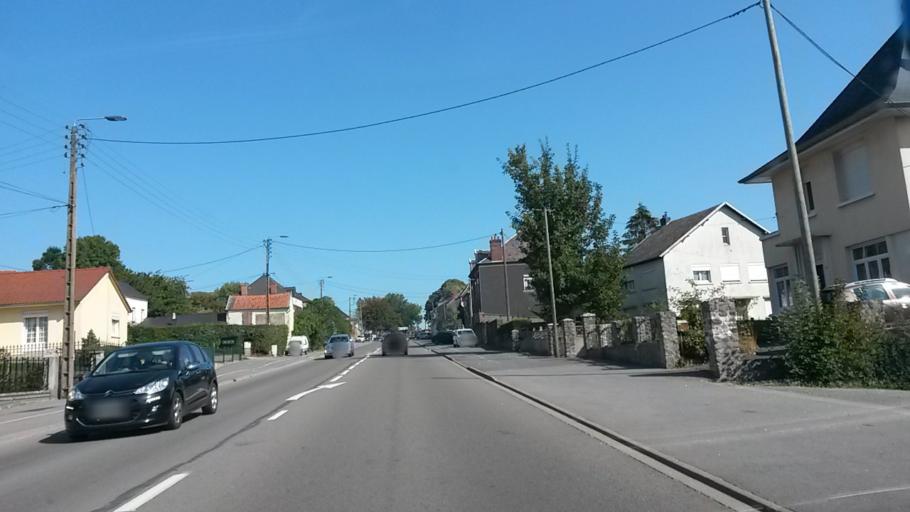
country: FR
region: Nord-Pas-de-Calais
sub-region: Departement du Nord
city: Avesnes-sur-Helpe
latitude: 50.1162
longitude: 3.9321
